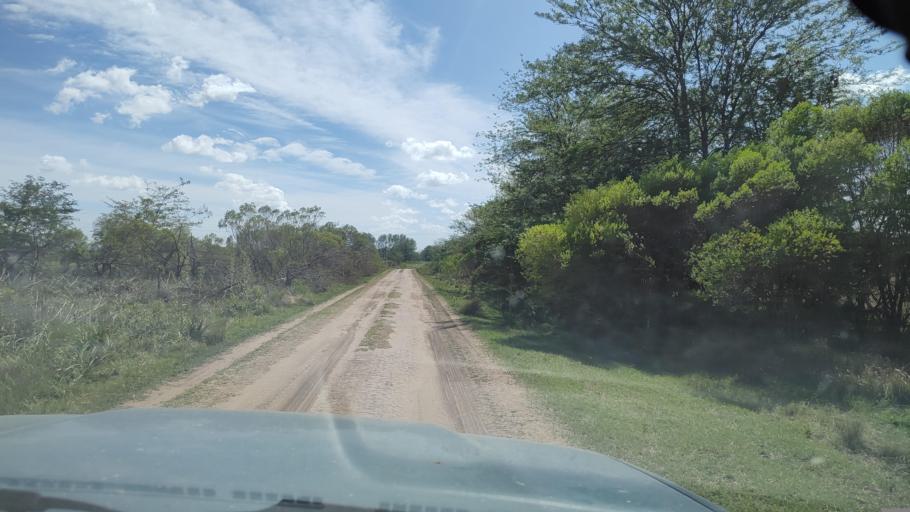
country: AR
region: Buenos Aires
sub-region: Partido de Lujan
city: Lujan
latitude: -34.5181
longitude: -59.1628
